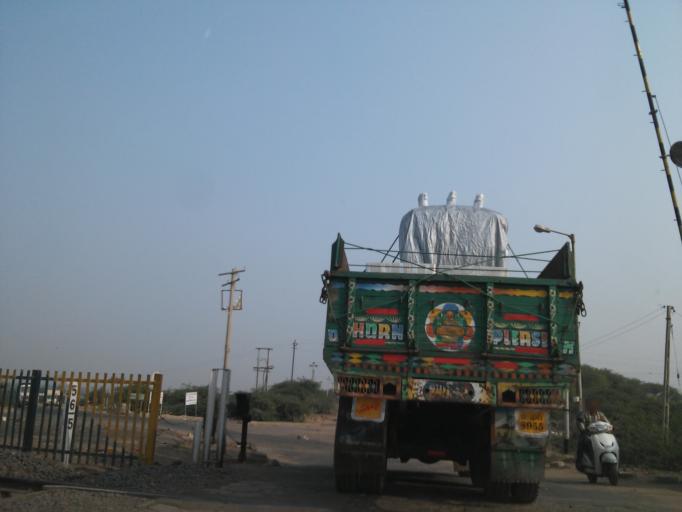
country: IN
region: Gujarat
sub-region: Kachchh
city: Bhuj
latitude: 23.2642
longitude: 69.6955
